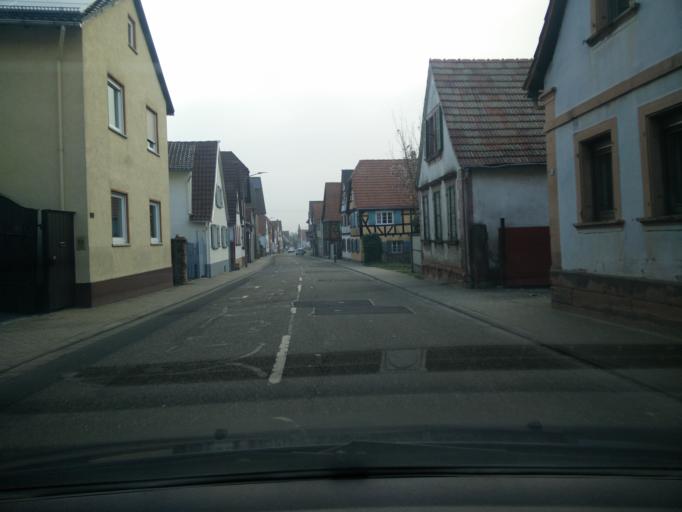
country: DE
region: Rheinland-Pfalz
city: Minfeld
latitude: 49.0722
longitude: 8.1417
